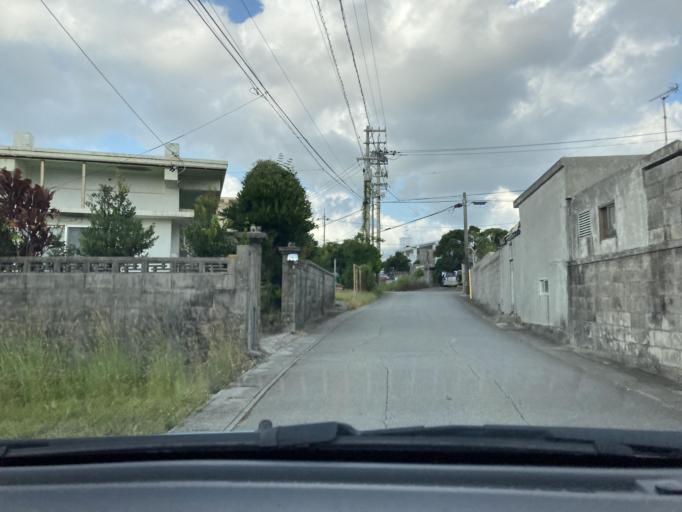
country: JP
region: Okinawa
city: Itoman
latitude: 26.0918
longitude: 127.6630
